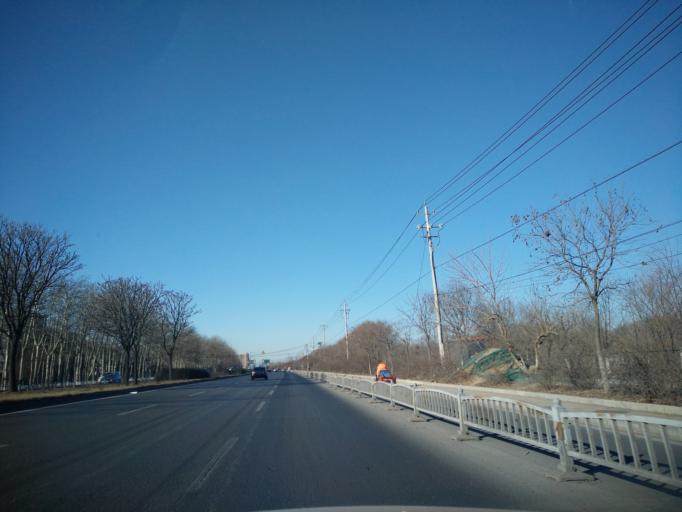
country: CN
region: Beijing
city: Xingfeng
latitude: 39.7207
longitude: 116.3669
